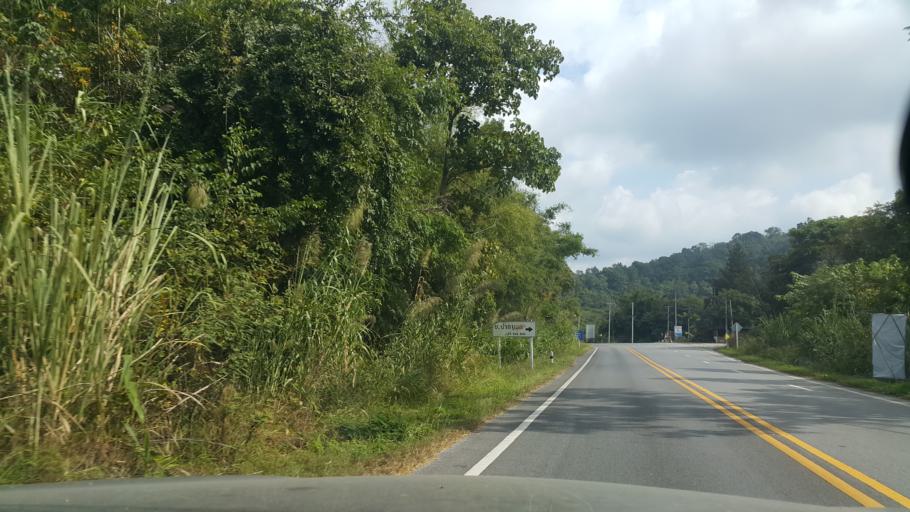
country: TH
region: Phayao
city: Phayao
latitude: 19.0614
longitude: 99.7767
